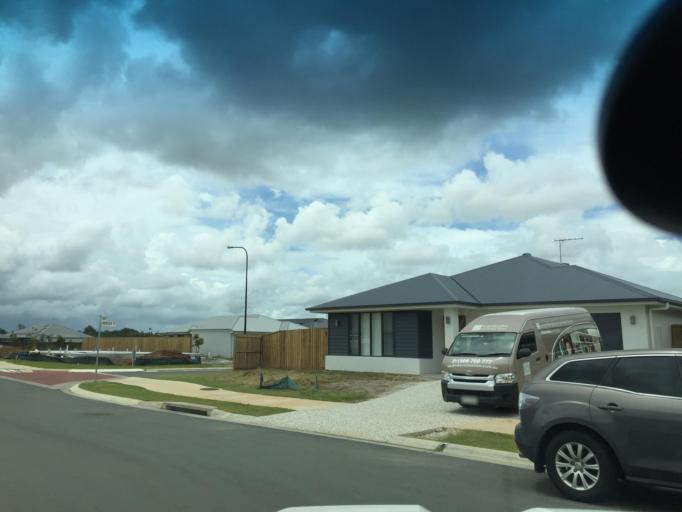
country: AU
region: Queensland
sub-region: Moreton Bay
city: Caboolture
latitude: -27.0637
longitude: 152.9248
